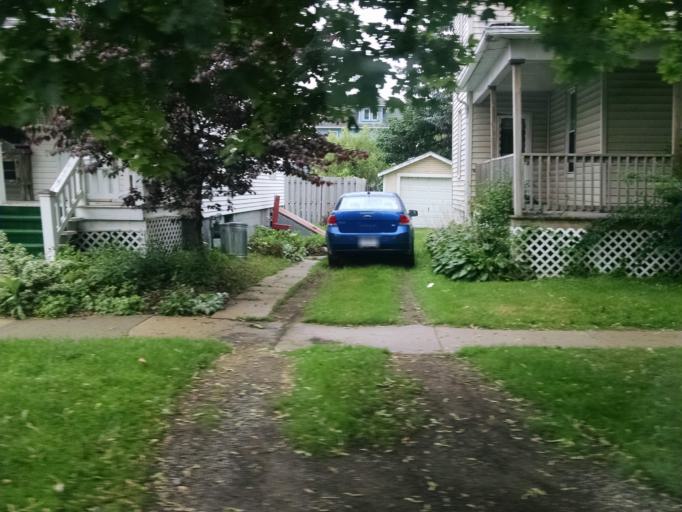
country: US
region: Pennsylvania
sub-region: Indiana County
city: Indiana
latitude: 40.6269
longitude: -79.1456
